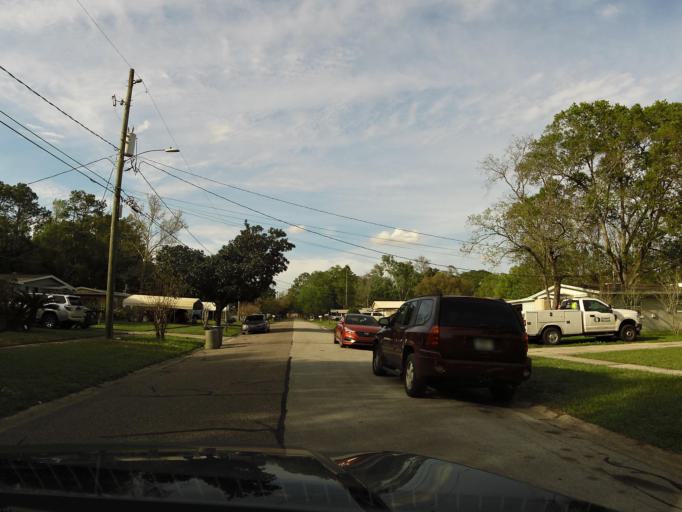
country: US
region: Florida
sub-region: Clay County
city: Bellair-Meadowbrook Terrace
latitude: 30.2380
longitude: -81.7608
